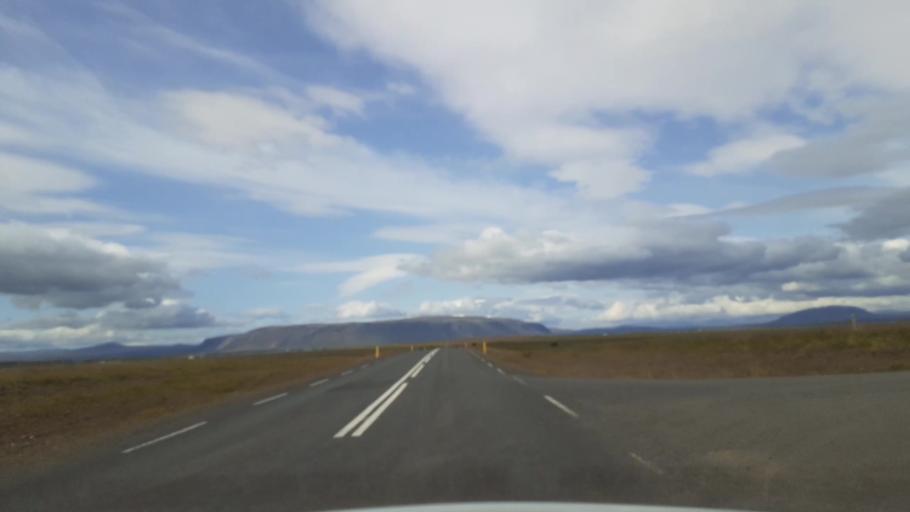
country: IS
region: South
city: Selfoss
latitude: 63.9038
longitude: -20.8140
